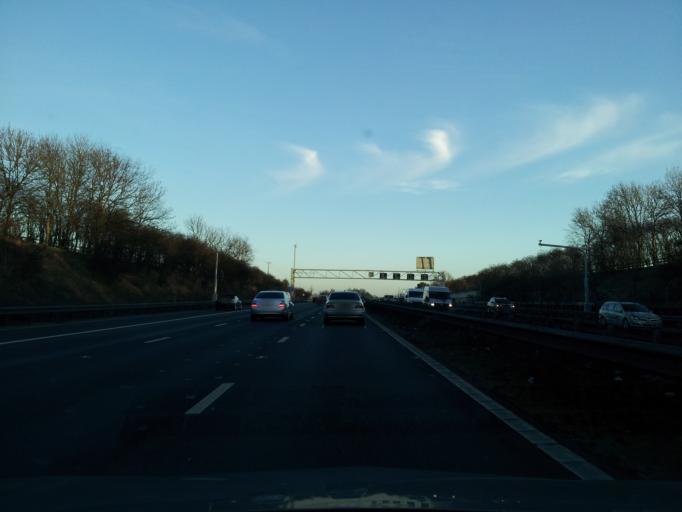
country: GB
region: England
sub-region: Central Bedfordshire
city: Ridgmont
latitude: 52.0158
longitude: -0.5626
